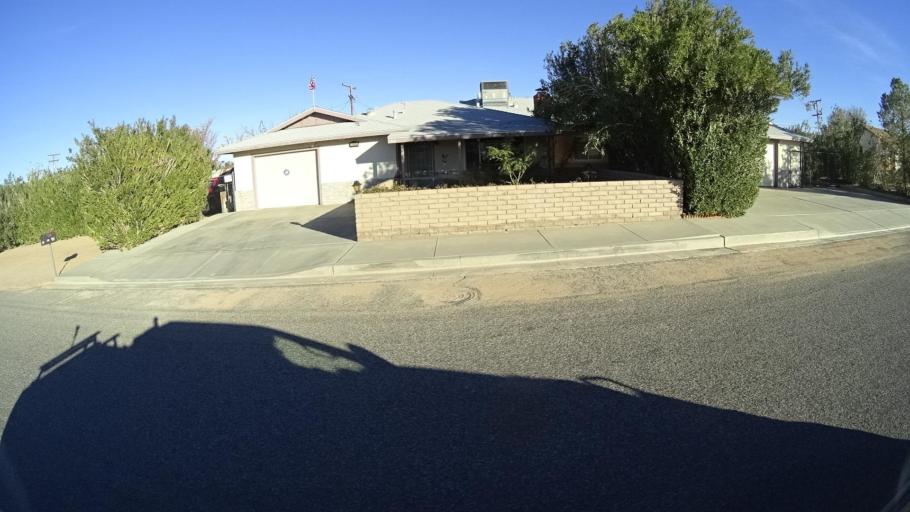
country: US
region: California
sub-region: Kern County
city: Ridgecrest
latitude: 35.5961
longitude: -117.6971
